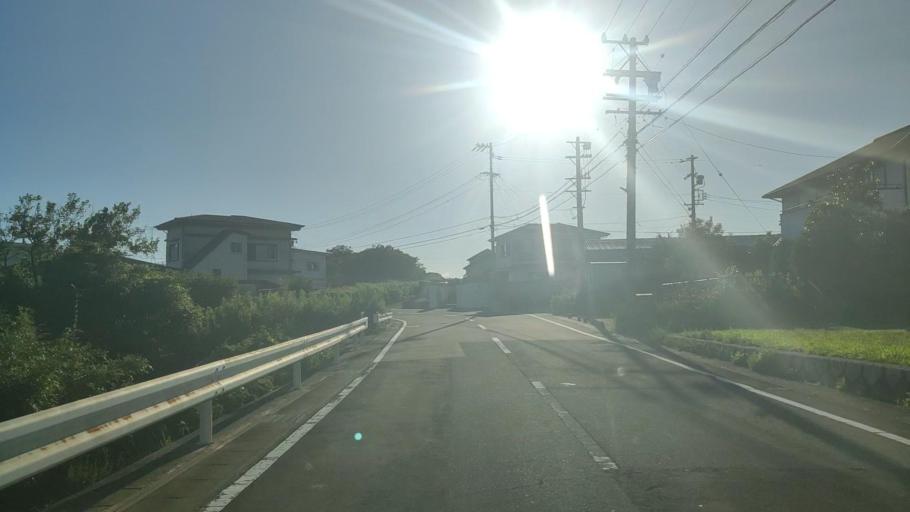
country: JP
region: Mie
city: Toba
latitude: 34.2868
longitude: 136.8895
